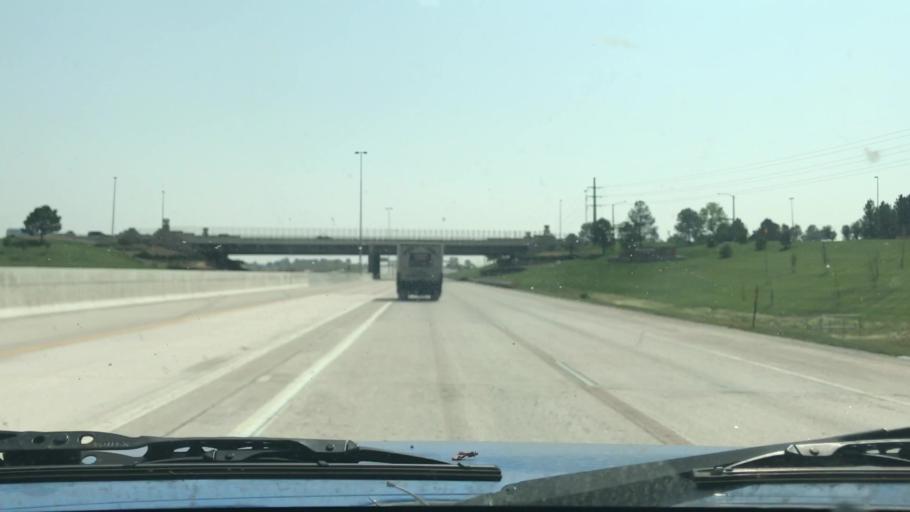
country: US
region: Colorado
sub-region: Boulder County
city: Louisville
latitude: 39.9356
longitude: -105.1293
